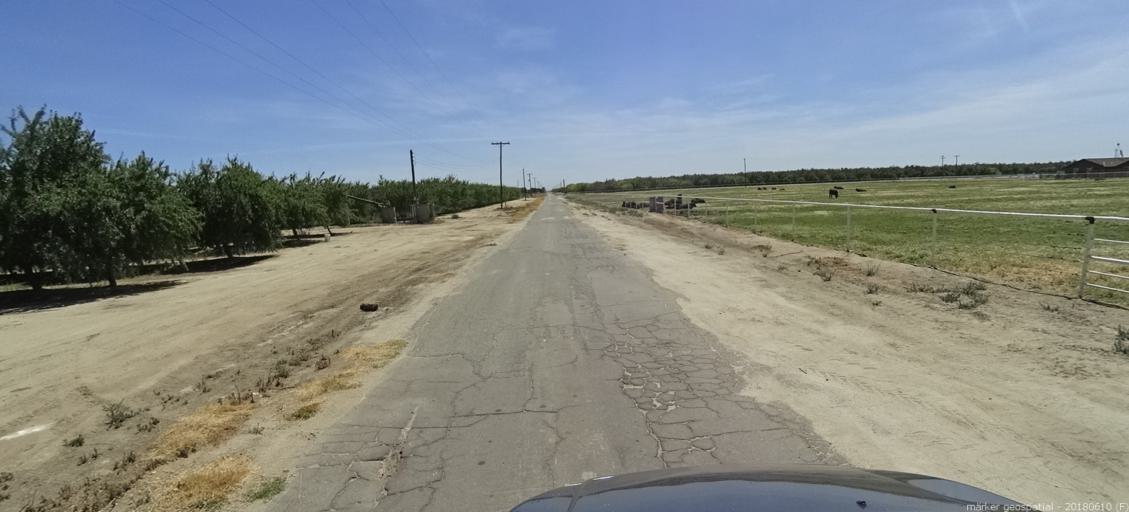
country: US
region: California
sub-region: Madera County
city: Chowchilla
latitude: 37.0471
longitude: -120.4039
